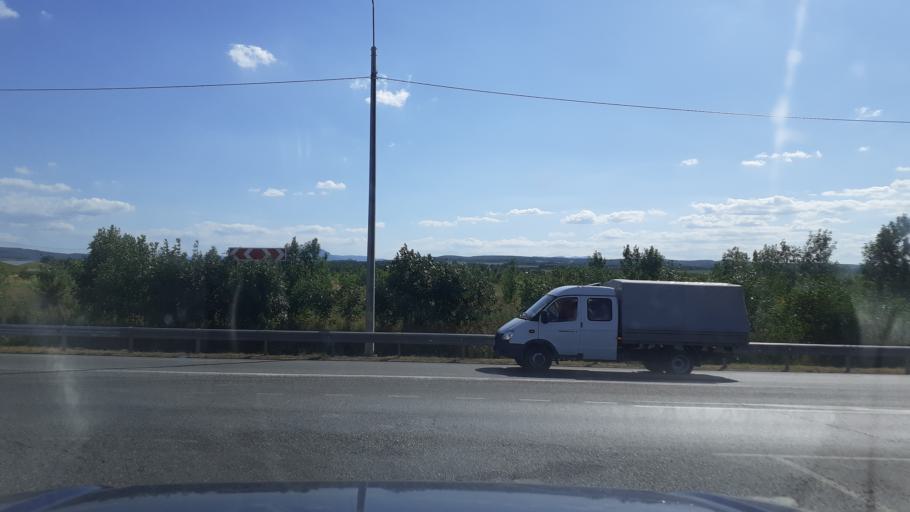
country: RU
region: Krasnodarskiy
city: Severskaya
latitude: 44.8436
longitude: 38.6568
